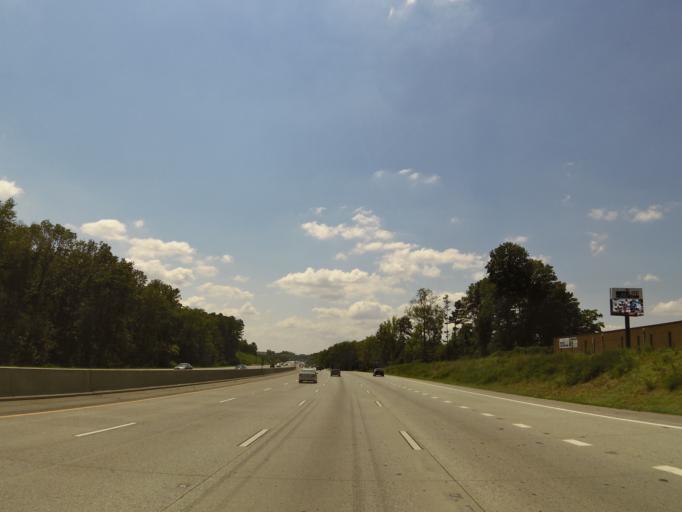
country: US
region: North Carolina
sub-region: Cabarrus County
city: Kannapolis
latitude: 35.4284
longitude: -80.6669
